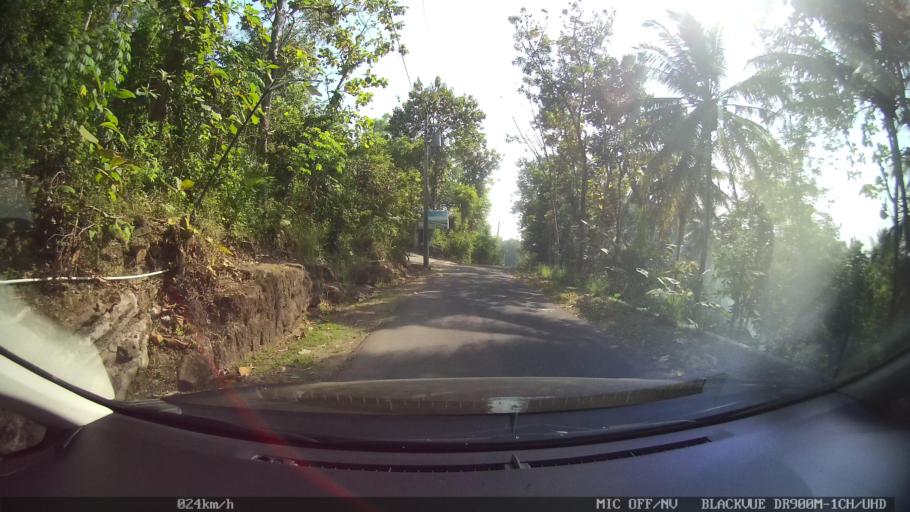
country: ID
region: Daerah Istimewa Yogyakarta
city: Kasihan
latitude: -7.8309
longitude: 110.2879
